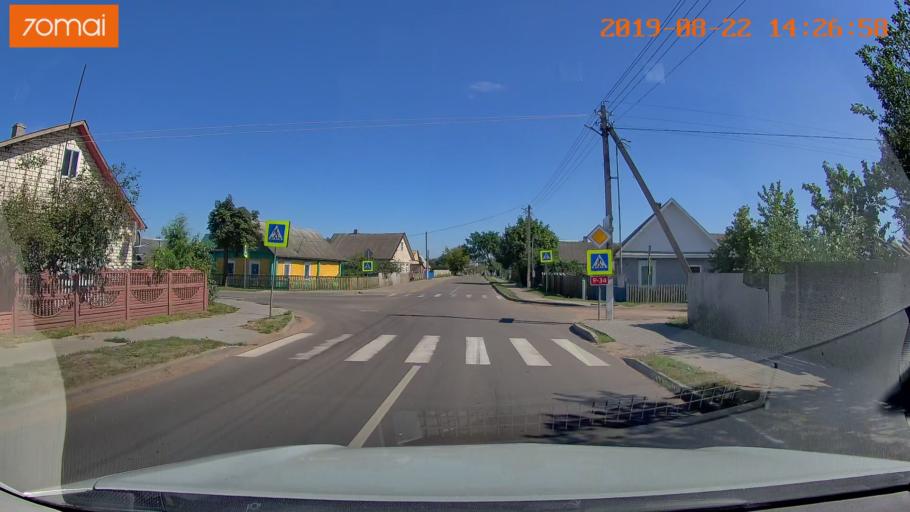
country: BY
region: Mogilev
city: Asipovichy
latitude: 53.2980
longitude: 28.6201
